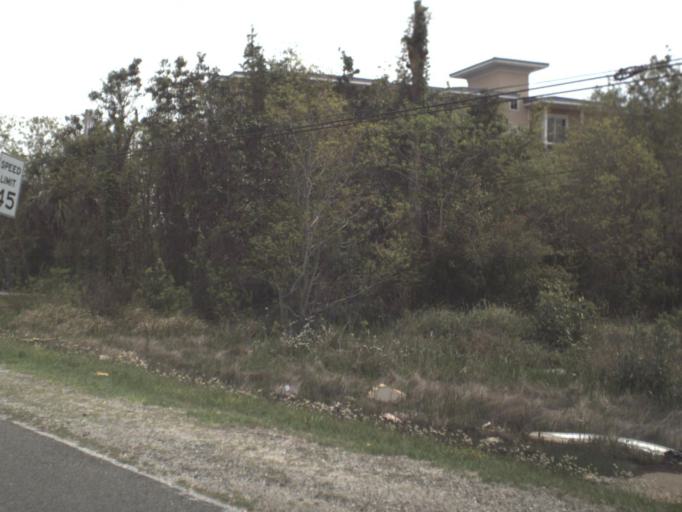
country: US
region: Florida
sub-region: Santa Rosa County
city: Navarre
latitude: 30.4020
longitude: -86.8580
